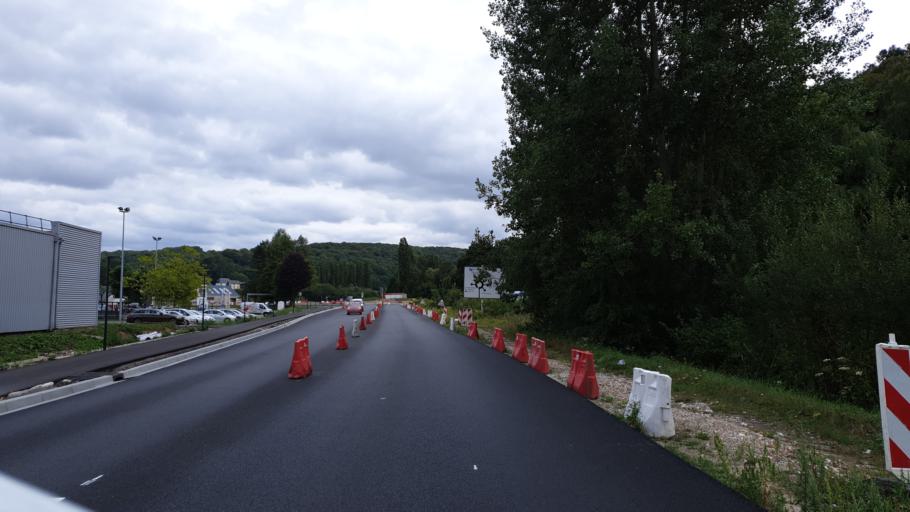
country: FR
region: Haute-Normandie
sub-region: Departement de la Seine-Maritime
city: Lillebonne
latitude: 49.5166
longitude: 0.5305
